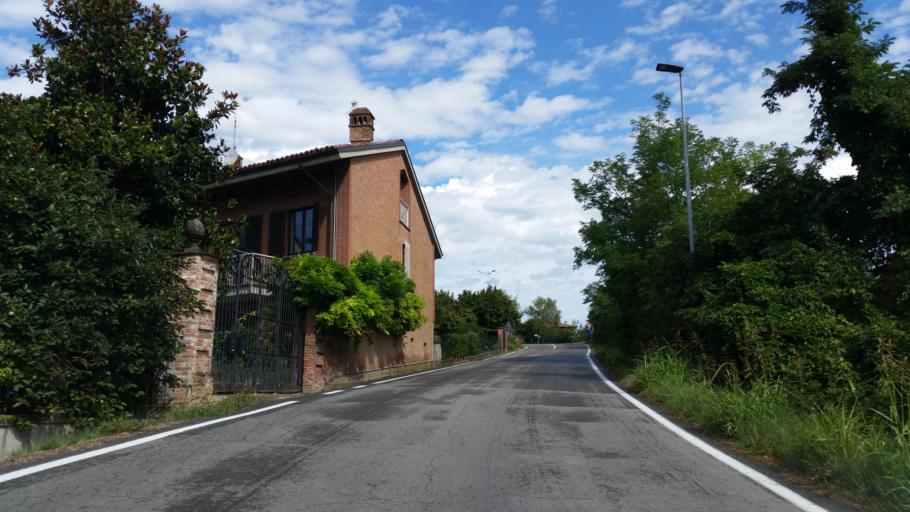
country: IT
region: Piedmont
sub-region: Provincia di Cuneo
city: Castagnito
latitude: 44.7559
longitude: 8.0342
